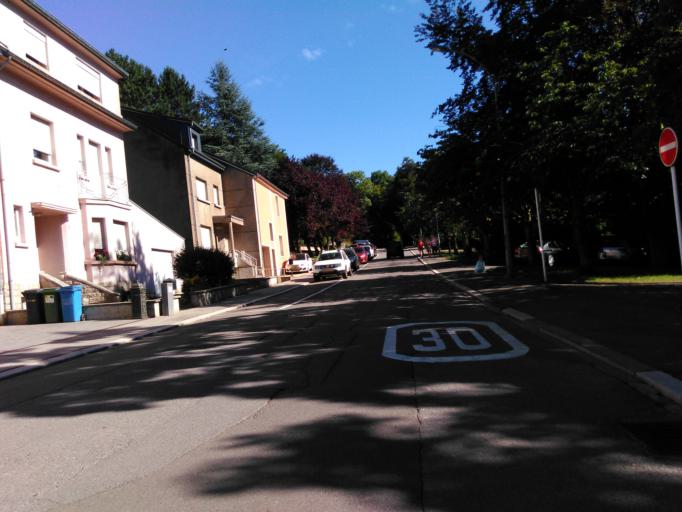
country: LU
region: Luxembourg
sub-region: Canton d'Esch-sur-Alzette
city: Sanem
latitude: 49.5464
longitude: 5.9257
